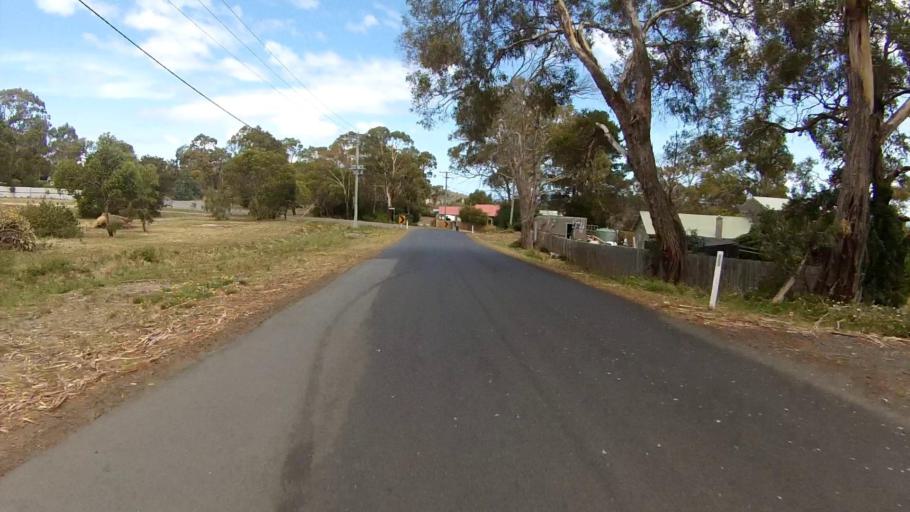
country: AU
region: Tasmania
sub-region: Sorell
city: Sorell
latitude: -42.8689
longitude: 147.6441
